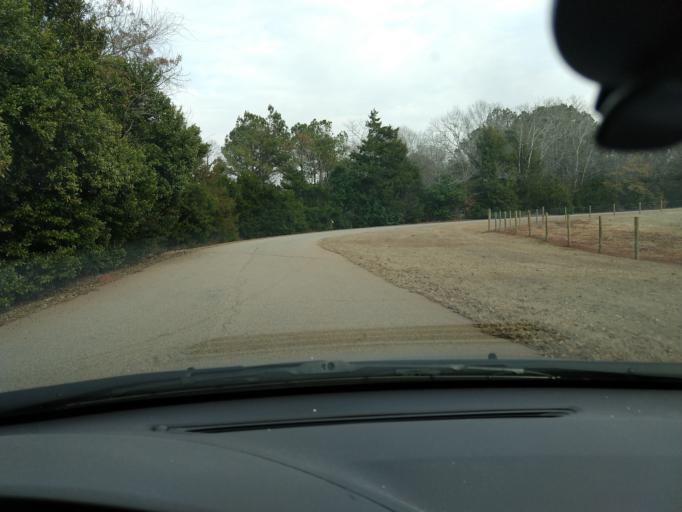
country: US
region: Georgia
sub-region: Webster County
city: Preston
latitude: 32.0266
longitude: -84.4311
